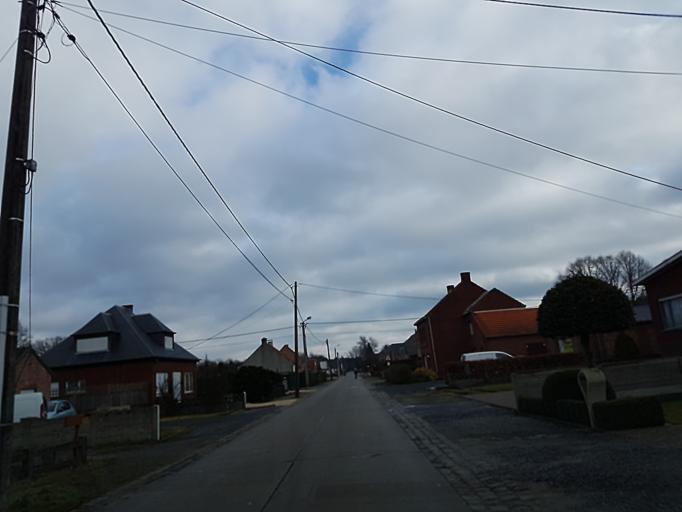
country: BE
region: Flanders
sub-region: Provincie Antwerpen
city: Hulshout
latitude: 51.0728
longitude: 4.8196
